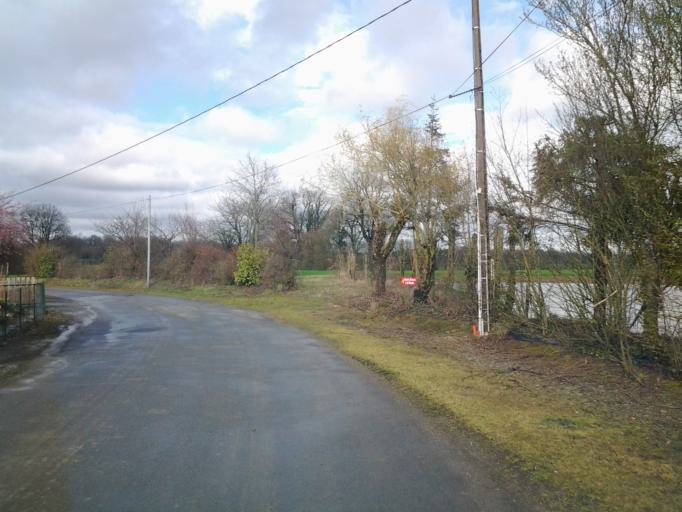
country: FR
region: Pays de la Loire
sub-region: Departement de la Vendee
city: Nesmy
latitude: 46.6439
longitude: -1.3626
